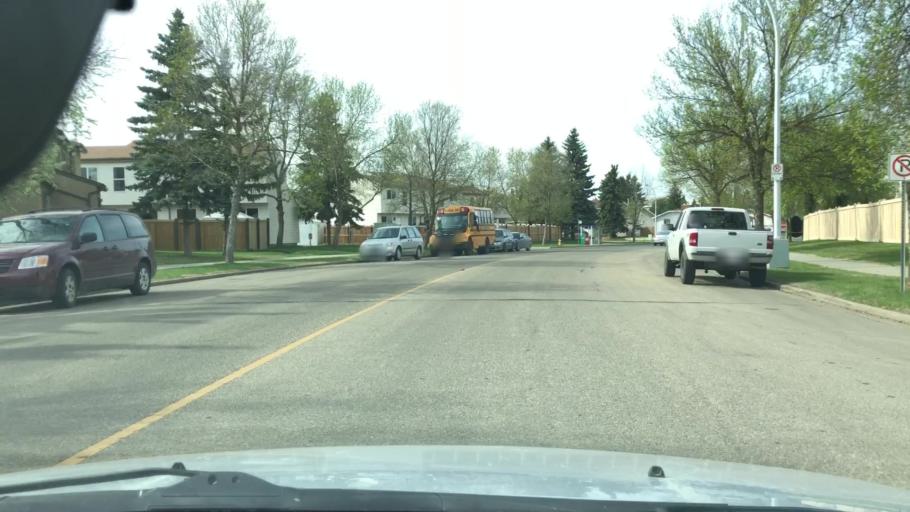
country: CA
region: Alberta
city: Edmonton
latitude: 53.6027
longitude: -113.5301
